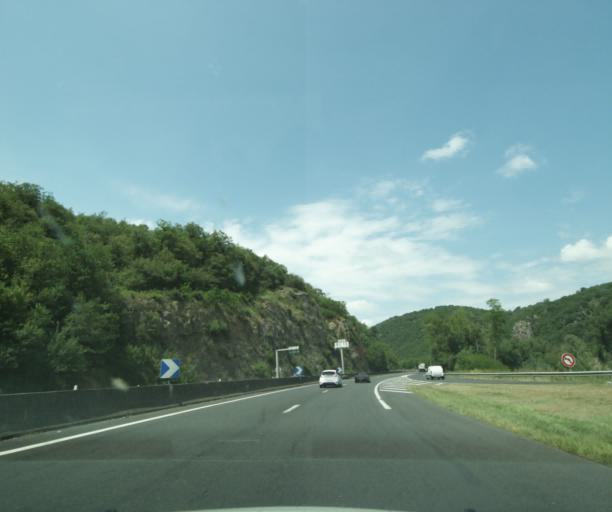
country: FR
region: Auvergne
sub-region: Departement du Puy-de-Dome
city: Issoire
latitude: 45.5670
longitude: 3.2497
